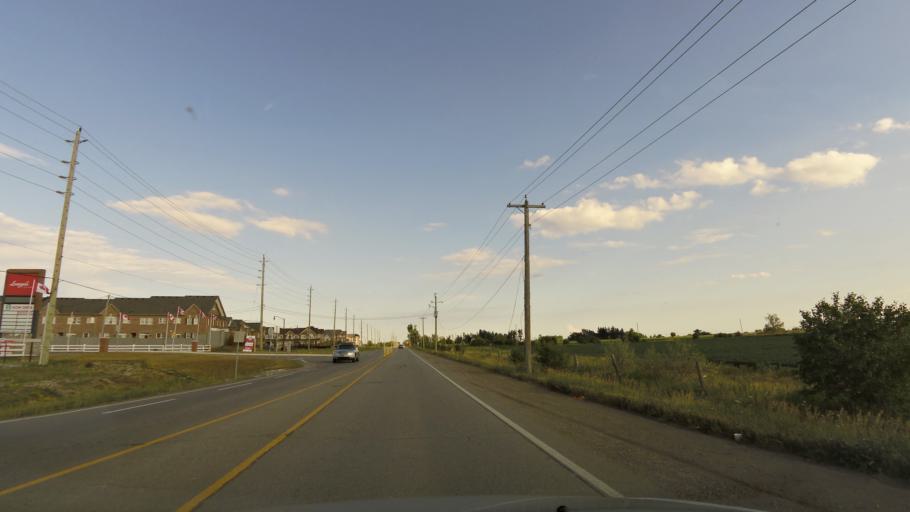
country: CA
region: Ontario
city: Brampton
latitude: 43.6783
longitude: -79.8451
